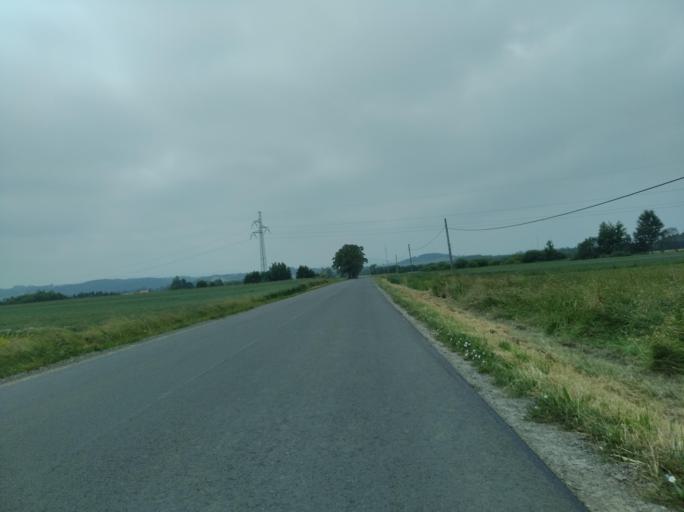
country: PL
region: Subcarpathian Voivodeship
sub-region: Powiat brzozowski
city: Haczow
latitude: 49.6224
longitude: 21.9060
